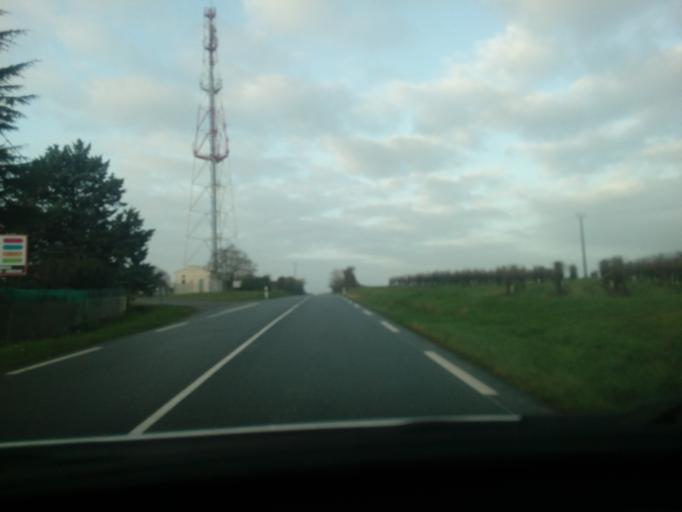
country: FR
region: Poitou-Charentes
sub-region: Departement de la Charente-Maritime
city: Jonzac
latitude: 45.4435
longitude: -0.4138
